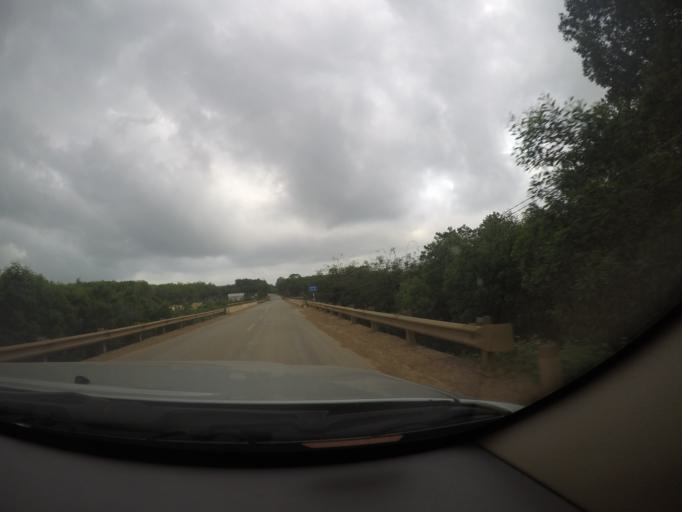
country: VN
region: Quang Tri
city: Ho Xa
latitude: 17.0351
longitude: 106.8956
